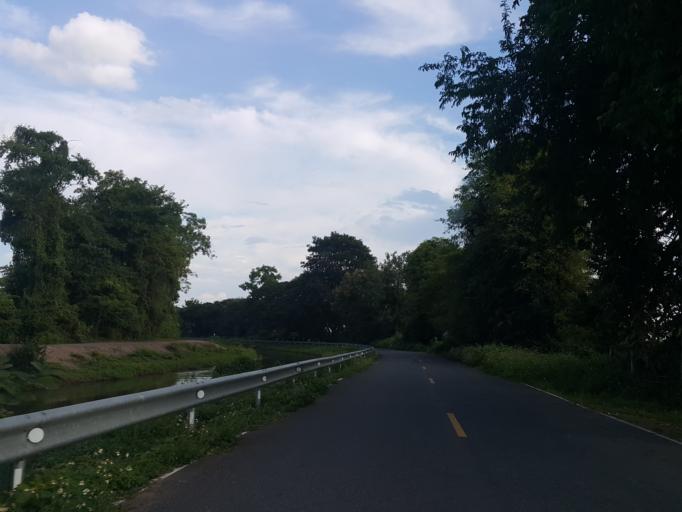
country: TH
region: Chiang Mai
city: Mae Taeng
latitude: 19.0613
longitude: 98.9662
